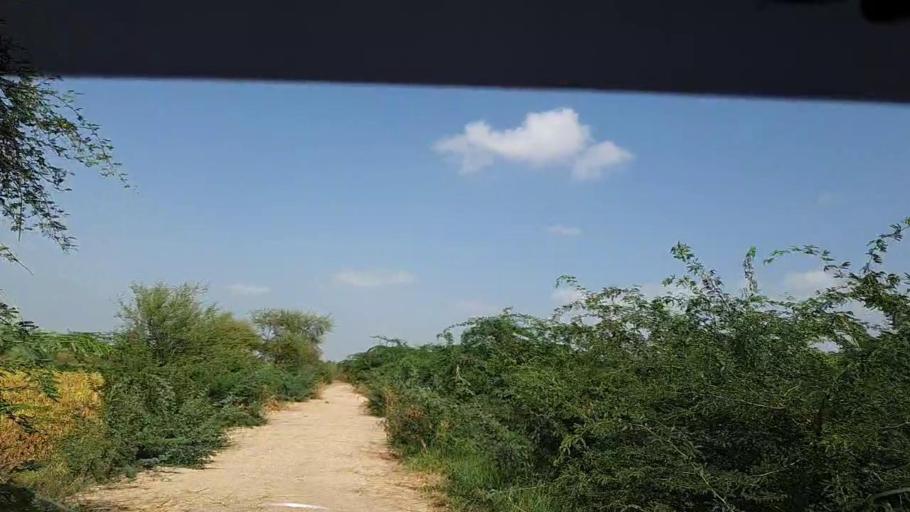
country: PK
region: Sindh
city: Badin
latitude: 24.5903
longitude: 68.8080
